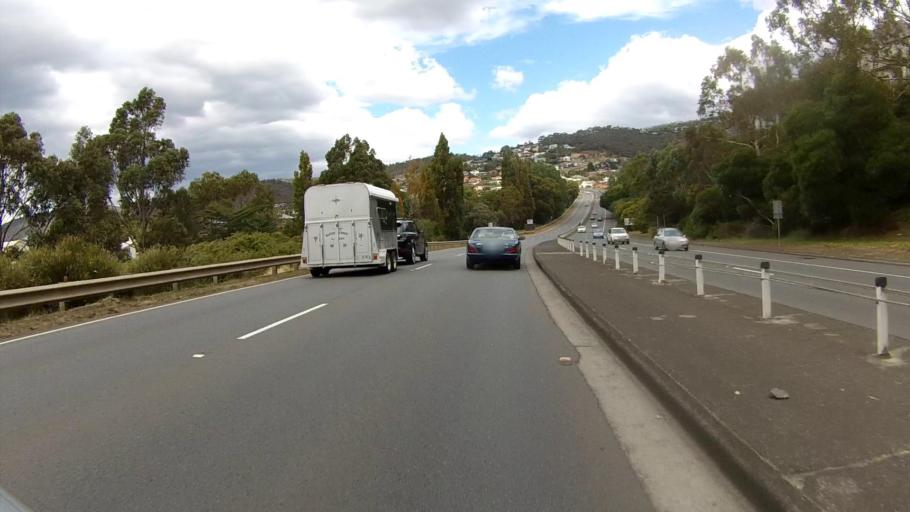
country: AU
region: Tasmania
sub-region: Hobart
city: Sandy Bay
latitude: -42.8952
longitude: 147.3181
